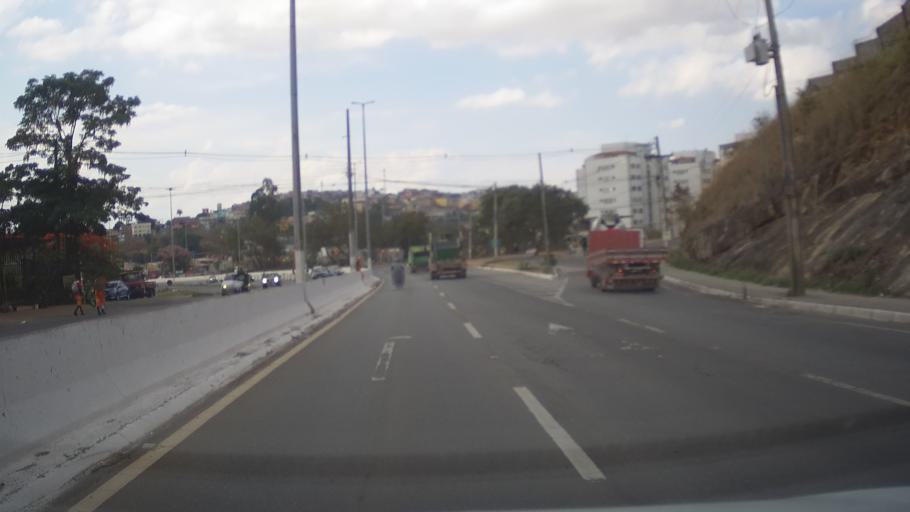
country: BR
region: Minas Gerais
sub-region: Belo Horizonte
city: Belo Horizonte
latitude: -19.8604
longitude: -43.8932
